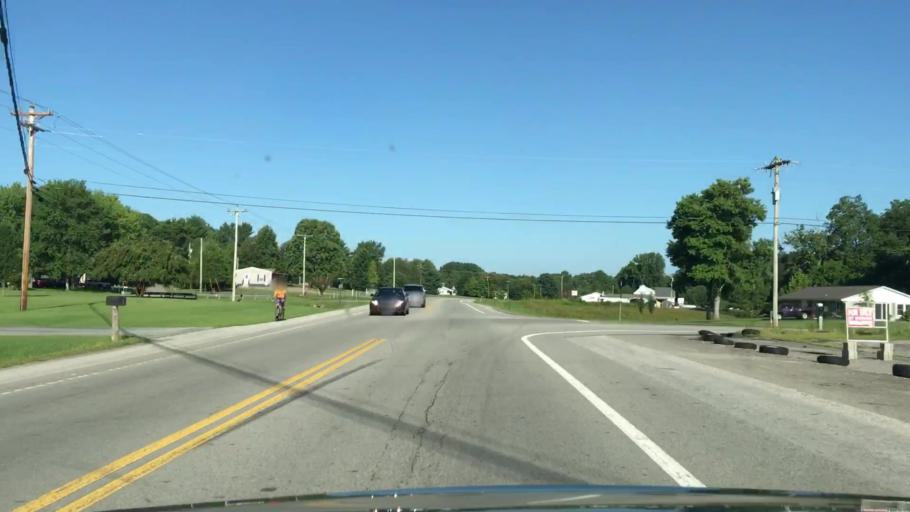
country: US
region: Tennessee
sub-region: Jackson County
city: Gainesboro
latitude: 36.2816
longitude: -85.6224
